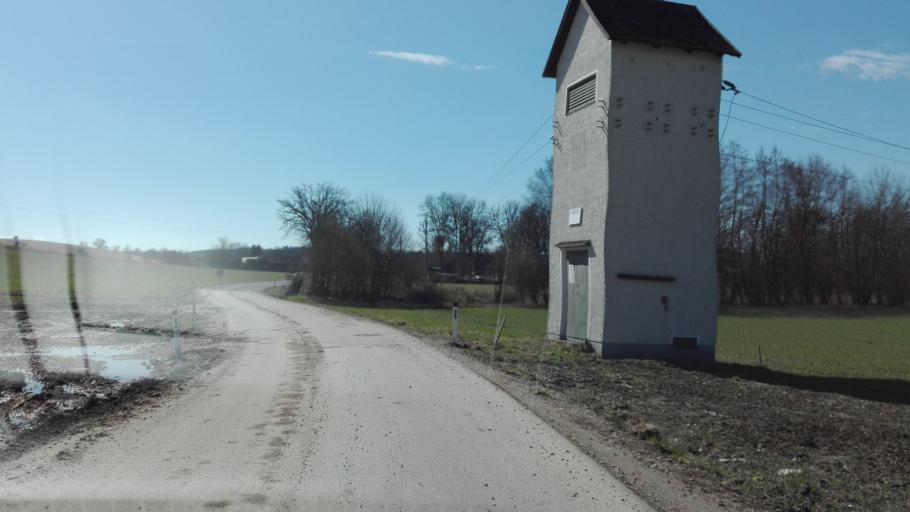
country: AT
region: Upper Austria
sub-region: Wels-Land
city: Buchkirchen
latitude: 48.2261
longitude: 13.9724
